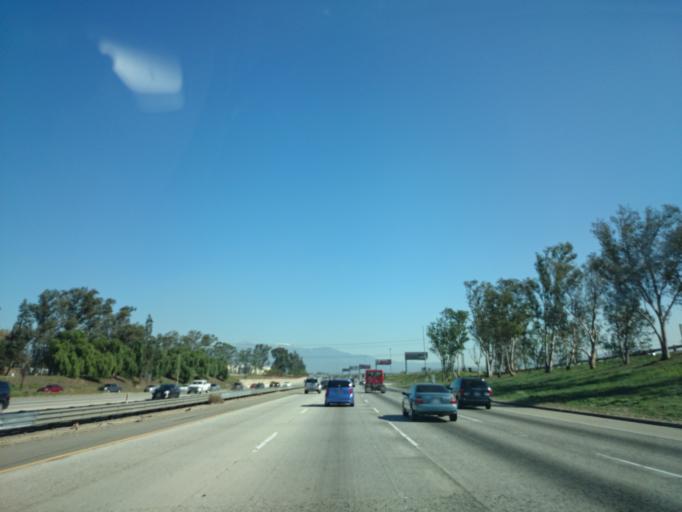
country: US
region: California
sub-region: San Bernardino County
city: Bloomington
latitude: 34.0684
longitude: -117.3943
